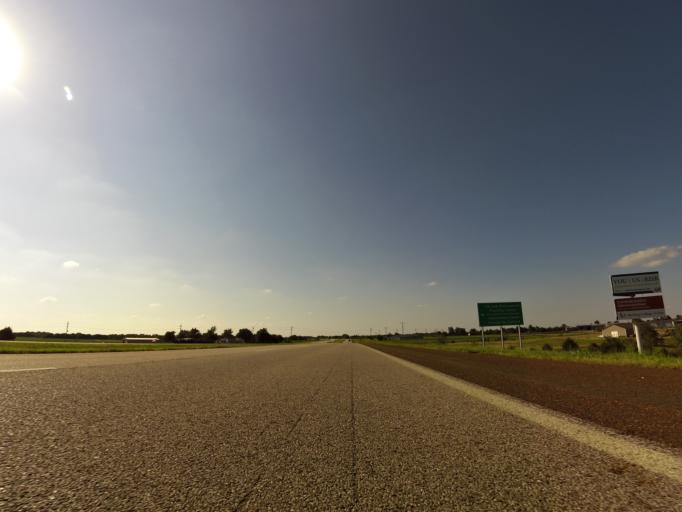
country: US
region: Kansas
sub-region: Reno County
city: South Hutchinson
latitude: 37.9423
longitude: -97.8823
